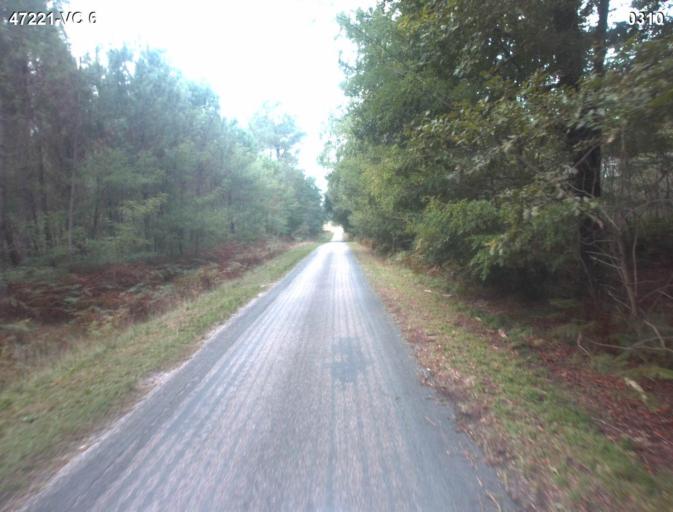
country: FR
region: Aquitaine
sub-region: Departement du Lot-et-Garonne
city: Mezin
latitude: 44.0977
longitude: 0.1760
